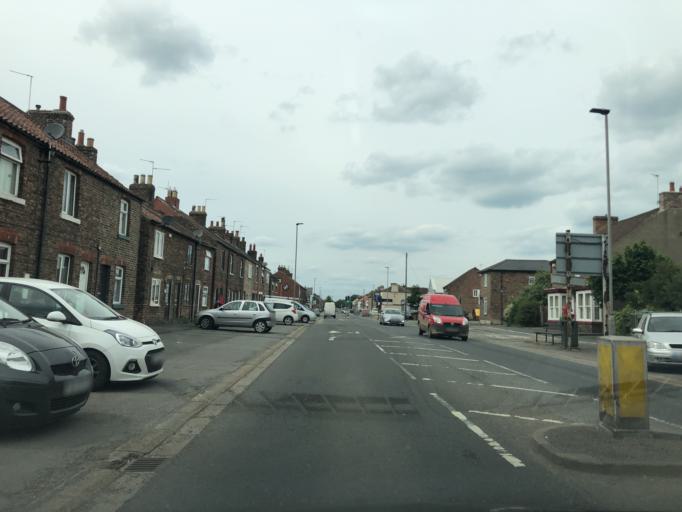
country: GB
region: England
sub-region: North Yorkshire
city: Thirsk
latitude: 54.2339
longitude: -1.3371
